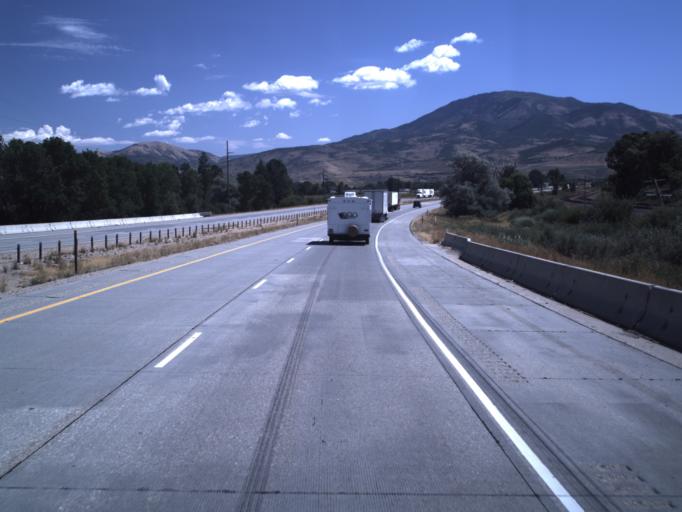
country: US
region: Utah
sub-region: Morgan County
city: Mountain Green
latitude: 41.1390
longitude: -111.8230
